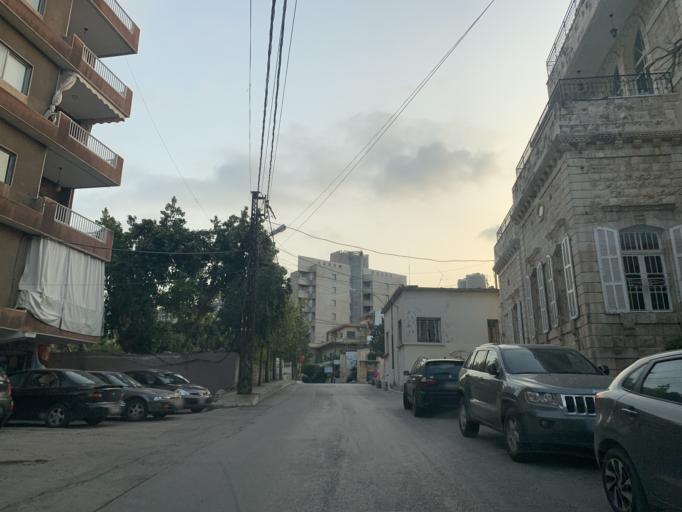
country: LB
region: Mont-Liban
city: Djounie
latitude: 33.9803
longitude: 35.6307
